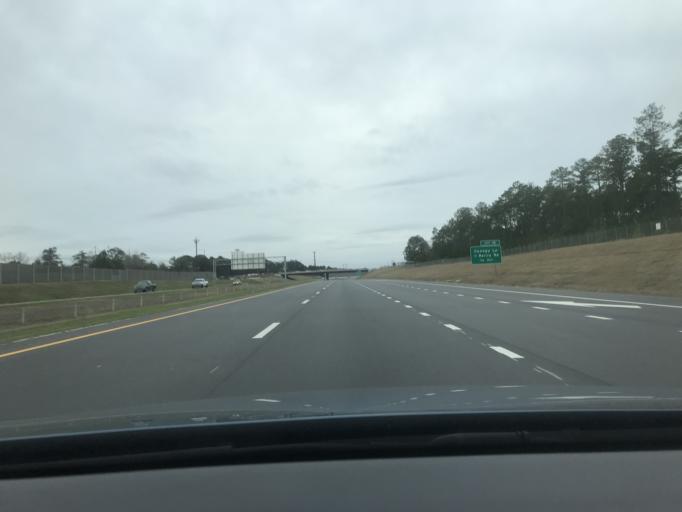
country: US
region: North Carolina
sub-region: Cumberland County
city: Fort Bragg
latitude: 35.1084
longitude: -78.9916
